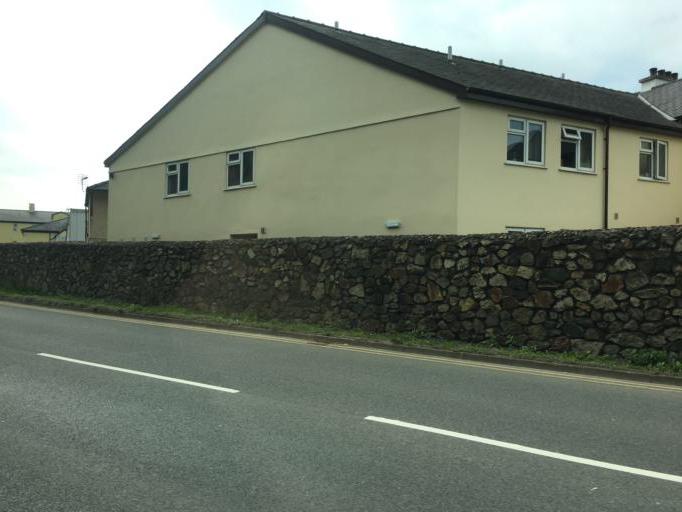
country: GB
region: Wales
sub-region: Gwynedd
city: Caernarfon
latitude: 53.1434
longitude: -4.2717
